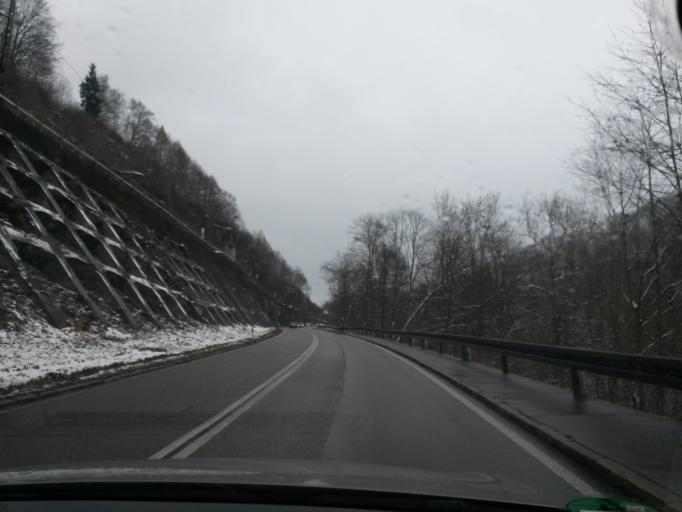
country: DE
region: Baden-Wuerttemberg
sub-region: Tuebingen Region
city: Amstetten
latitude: 48.5907
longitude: 9.8597
